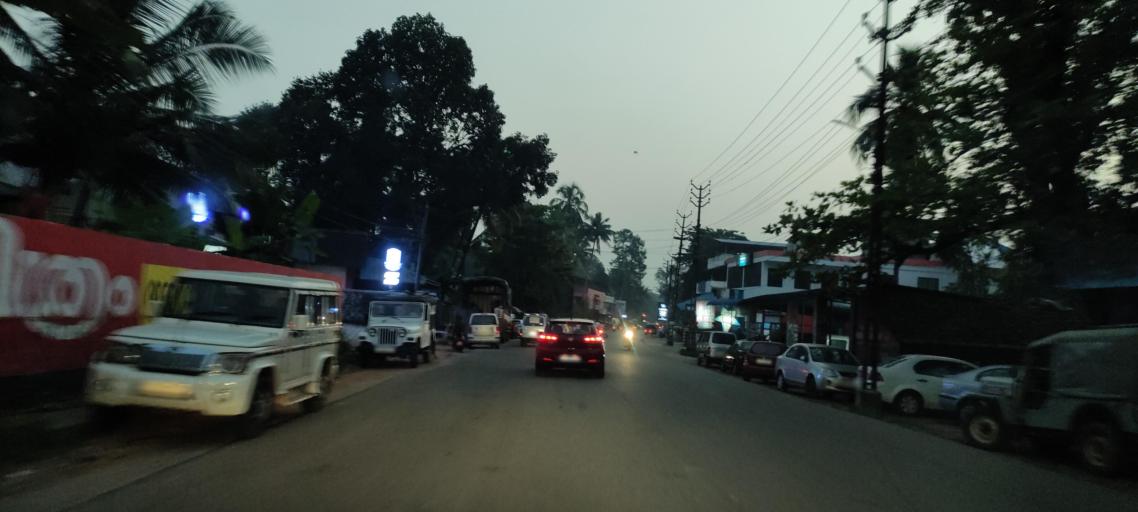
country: IN
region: Kerala
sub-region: Pattanamtitta
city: Adur
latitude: 9.1495
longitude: 76.7336
